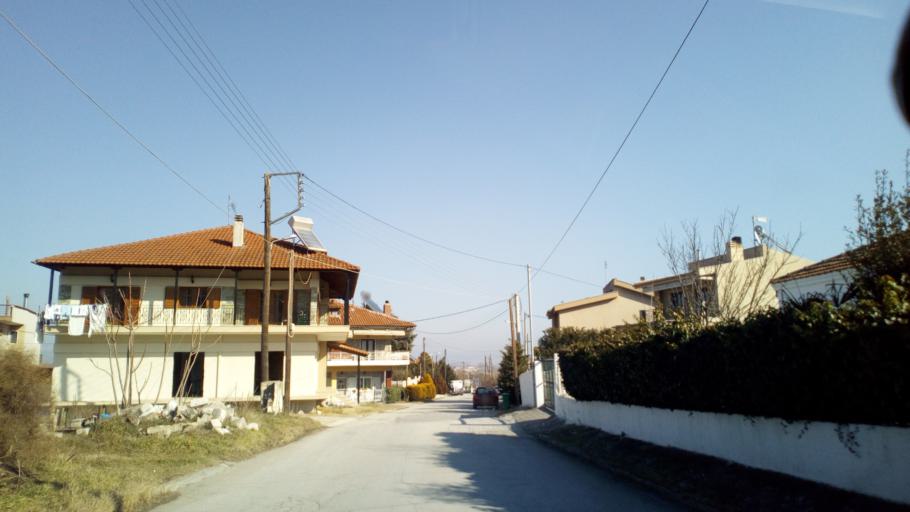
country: GR
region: Central Macedonia
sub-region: Nomos Thessalonikis
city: Lagyna
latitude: 40.7256
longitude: 23.0075
